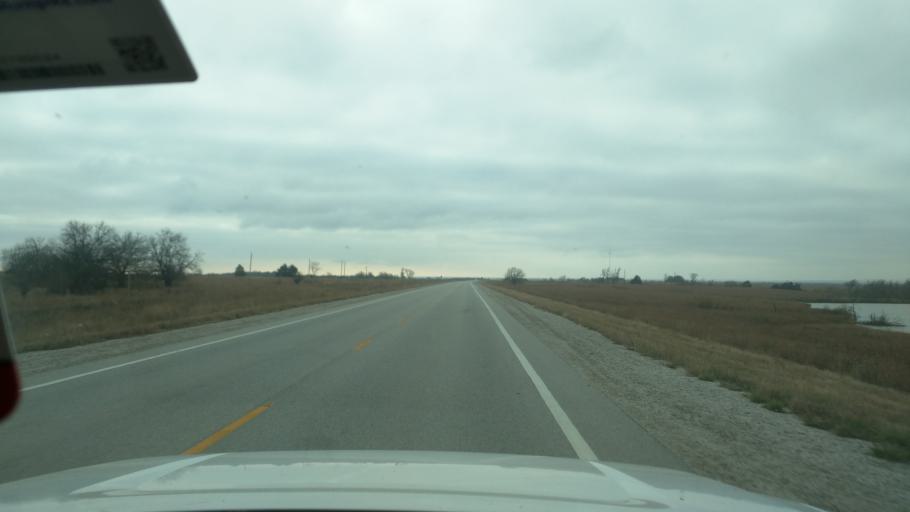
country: US
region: Kansas
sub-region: Elk County
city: Howard
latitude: 37.5660
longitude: -96.2532
